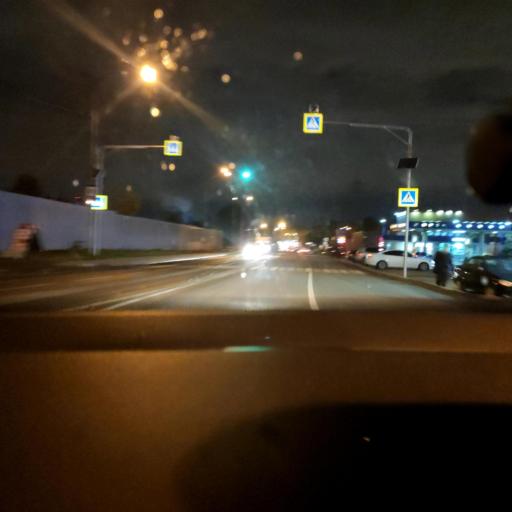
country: RU
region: Moskovskaya
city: Kotel'niki
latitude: 55.6394
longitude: 37.8438
